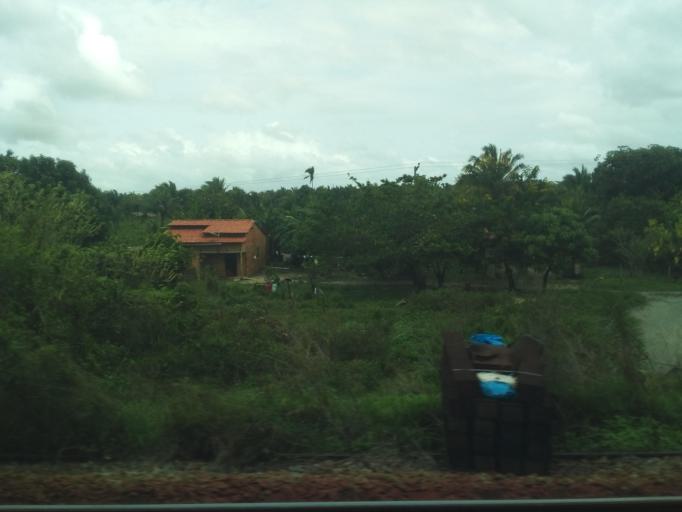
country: BR
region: Maranhao
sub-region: Arari
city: Arari
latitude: -3.5750
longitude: -44.7393
